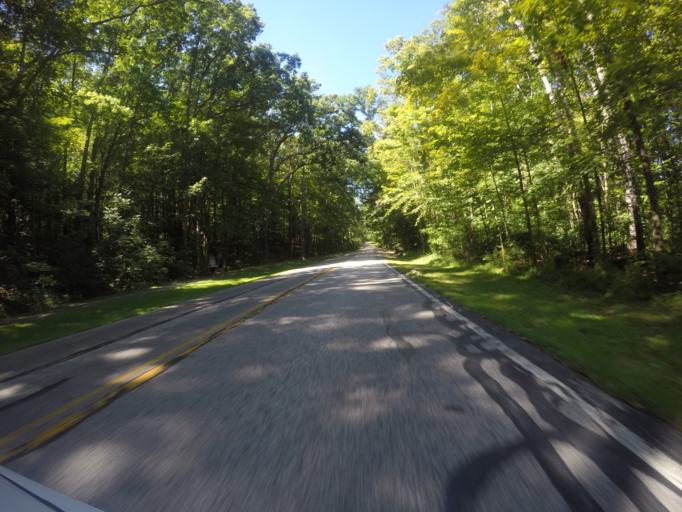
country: US
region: Ohio
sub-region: Cuyahoga County
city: Brecksville
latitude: 41.3032
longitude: -81.6128
